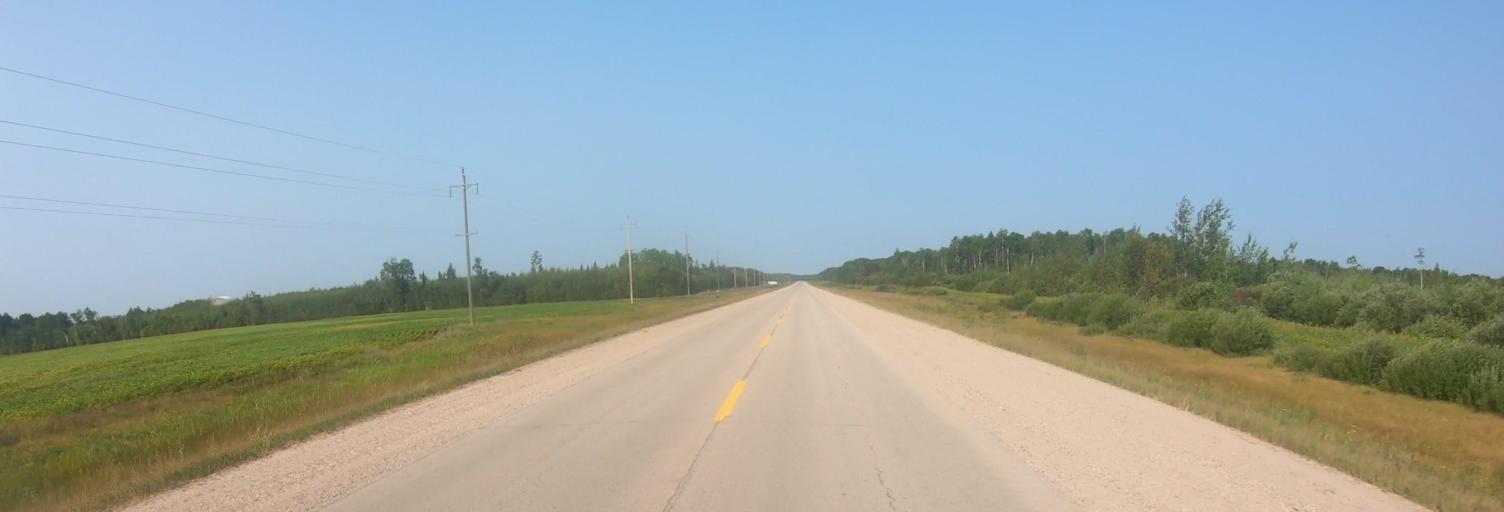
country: US
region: Minnesota
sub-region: Roseau County
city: Roseau
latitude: 49.0234
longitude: -95.7077
